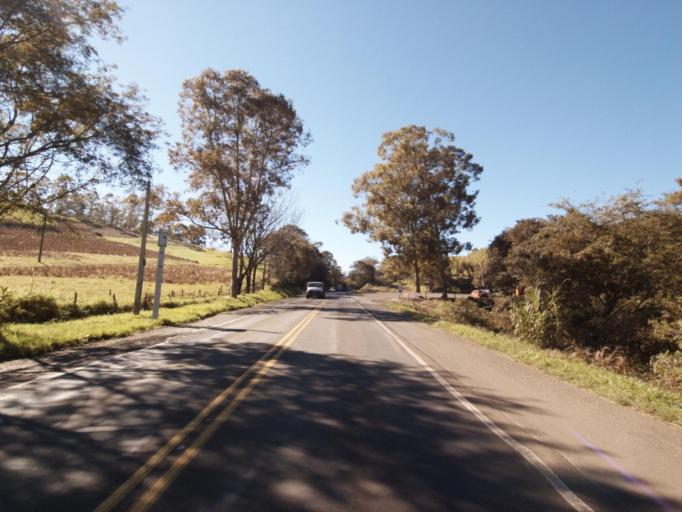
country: BR
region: Rio Grande do Sul
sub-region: Frederico Westphalen
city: Frederico Westphalen
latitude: -26.7983
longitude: -53.3442
